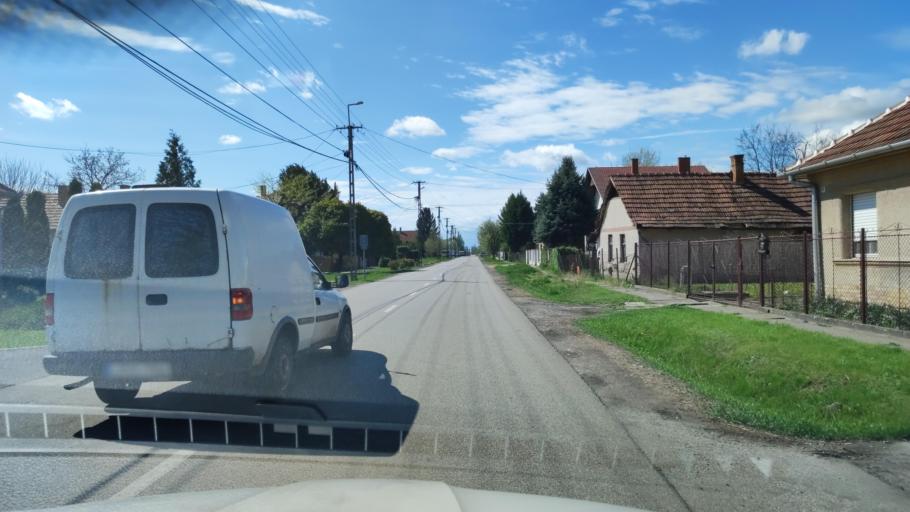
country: HU
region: Pest
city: Abony
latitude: 47.1805
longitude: 20.0060
